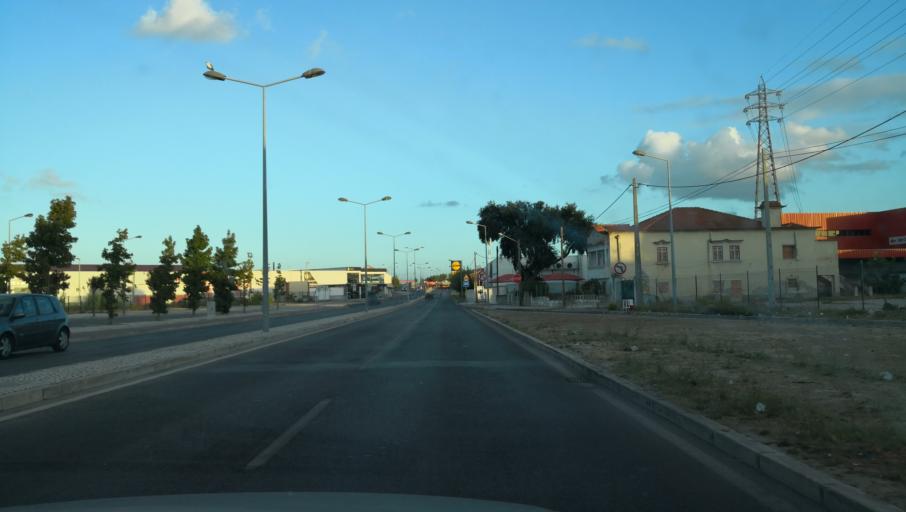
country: PT
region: Setubal
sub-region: Moita
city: Alhos Vedros
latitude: 38.6577
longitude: -9.0380
